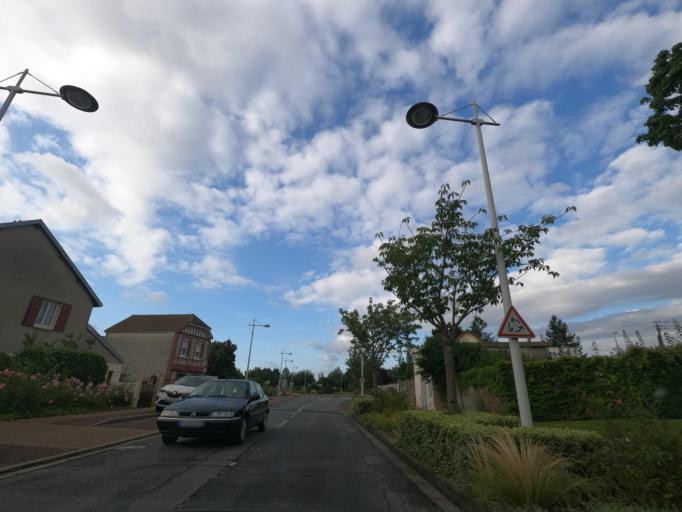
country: FR
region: Haute-Normandie
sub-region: Departement de la Seine-Maritime
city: Grand-Couronne
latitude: 49.3635
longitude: 1.0132
